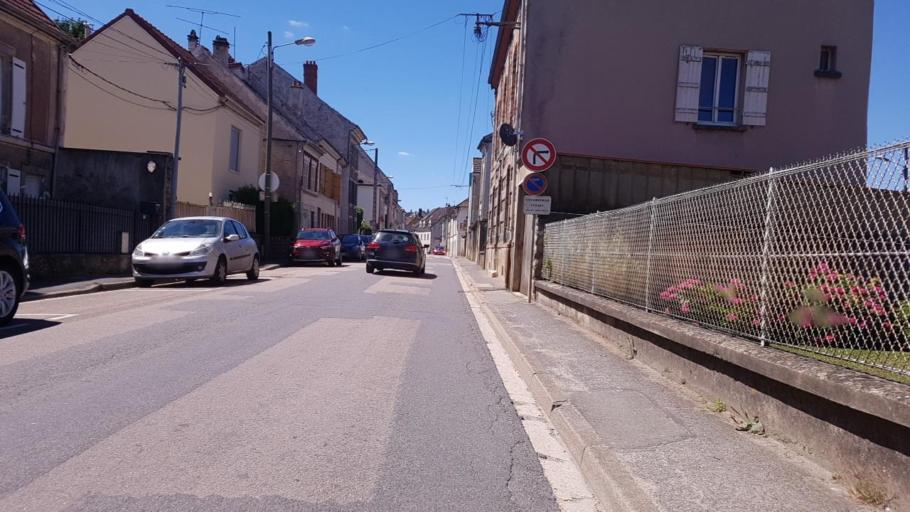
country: FR
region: Ile-de-France
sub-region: Departement de Seine-et-Marne
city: La Ferte-sous-Jouarre
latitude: 48.9495
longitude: 3.1351
